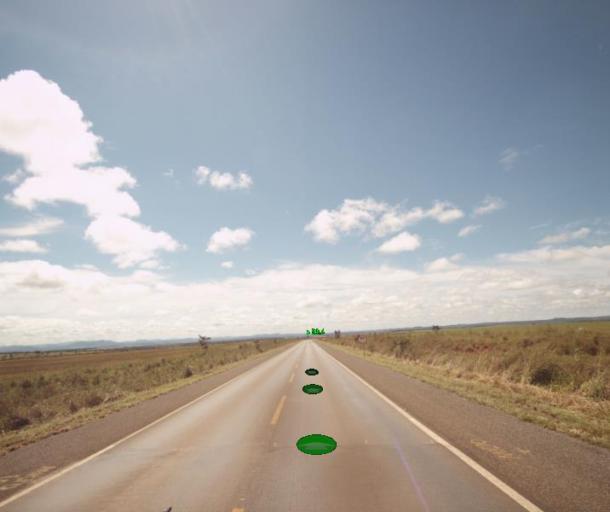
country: BR
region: Goias
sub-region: Padre Bernardo
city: Padre Bernardo
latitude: -15.1737
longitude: -48.3953
